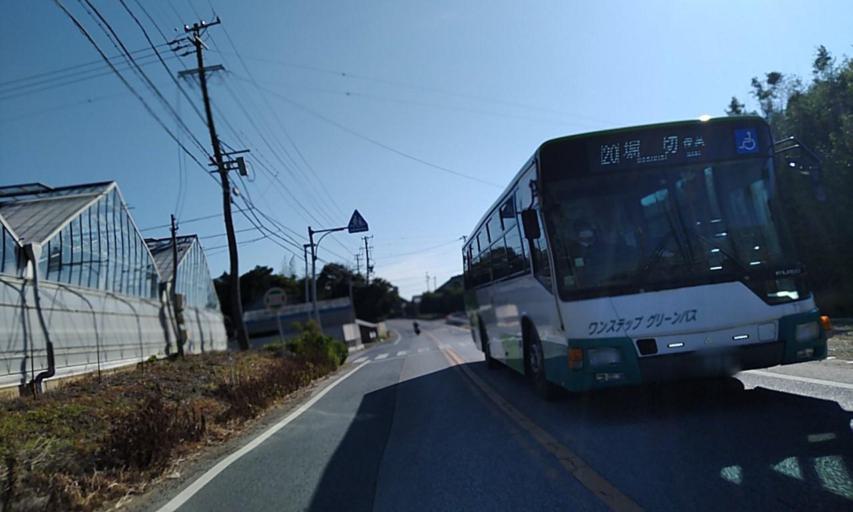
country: JP
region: Aichi
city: Tahara
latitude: 34.5928
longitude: 137.0953
